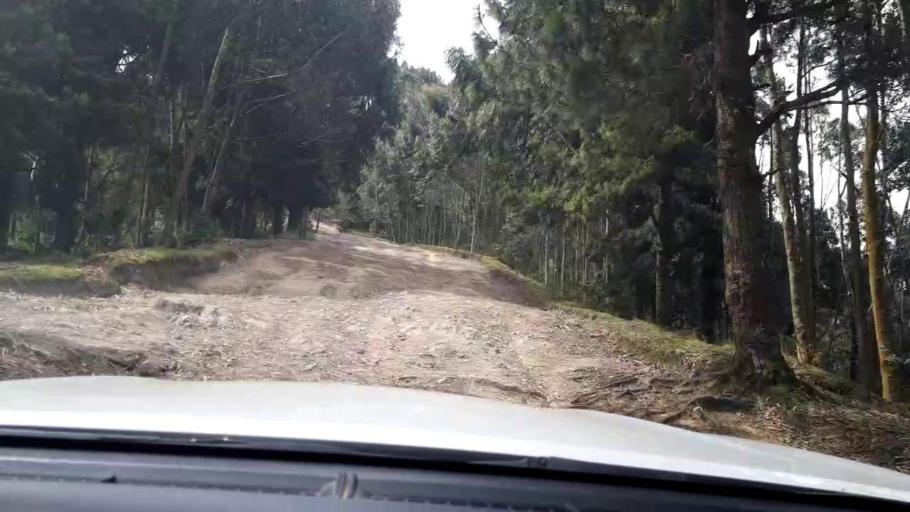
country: RW
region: Western Province
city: Kibuye
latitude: -1.8730
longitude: 29.4529
